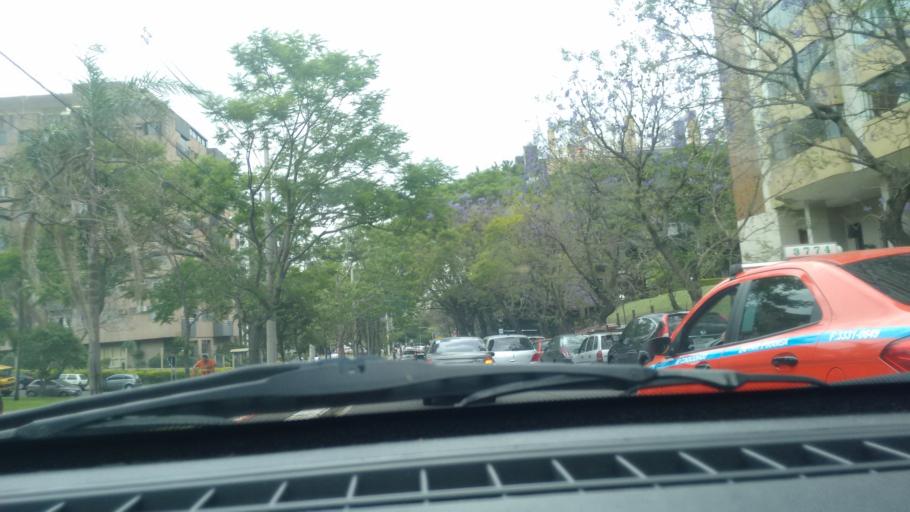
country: BR
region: Rio Grande do Sul
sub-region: Porto Alegre
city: Porto Alegre
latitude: -30.0385
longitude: -51.1925
